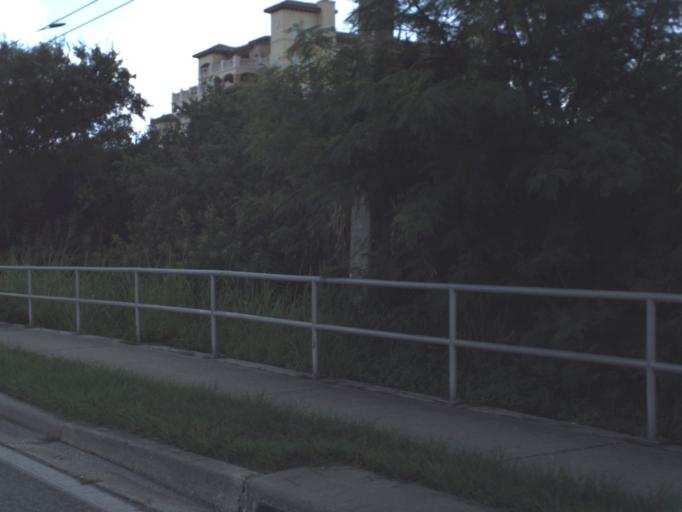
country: US
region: Florida
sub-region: Sarasota County
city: South Sarasota
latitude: 27.2753
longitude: -82.5308
